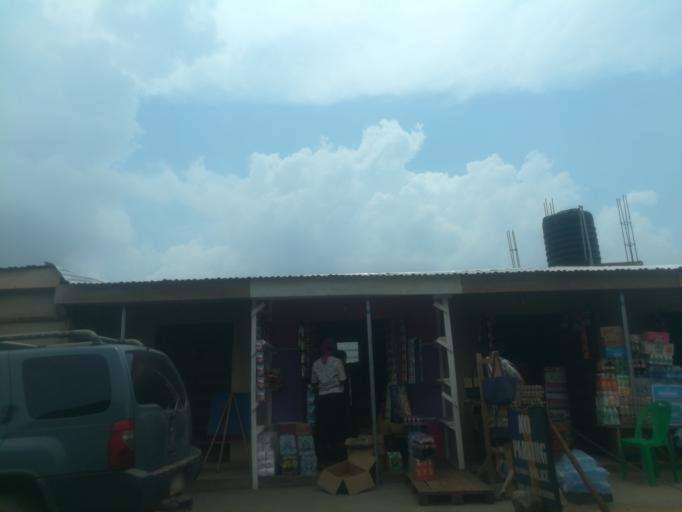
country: NG
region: Oyo
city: Ibadan
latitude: 7.4304
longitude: 3.9219
